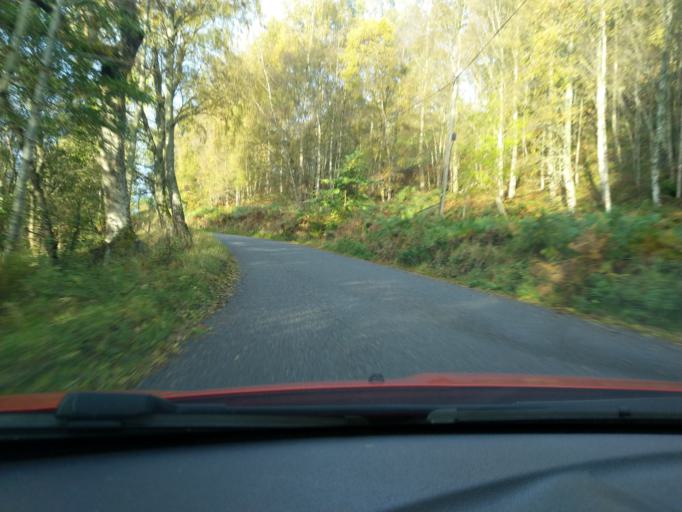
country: GB
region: Scotland
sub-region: Perth and Kinross
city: Aberfeldy
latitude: 56.7019
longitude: -4.1404
